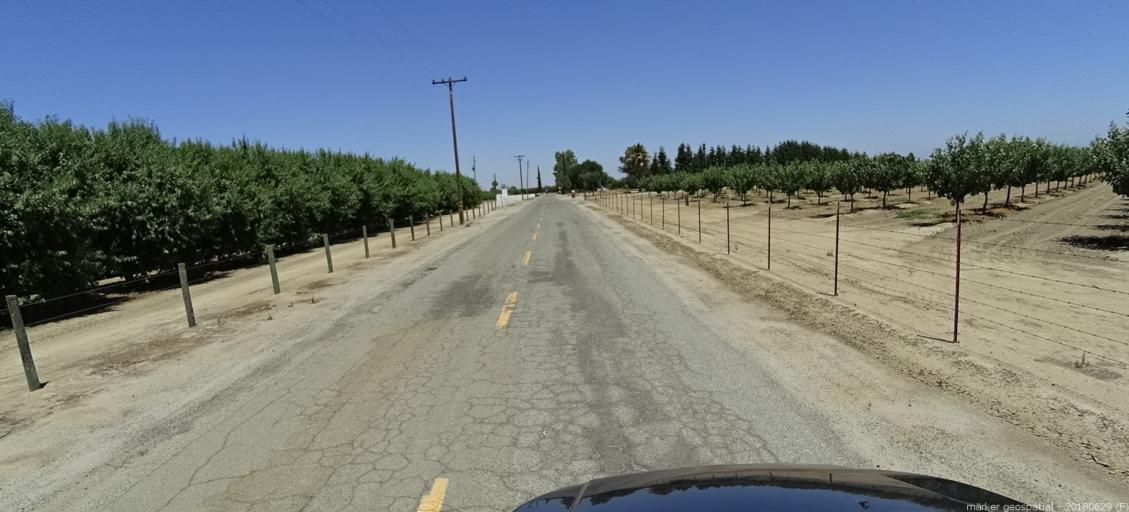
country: US
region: California
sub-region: Madera County
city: Parksdale
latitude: 37.0072
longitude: -119.9912
